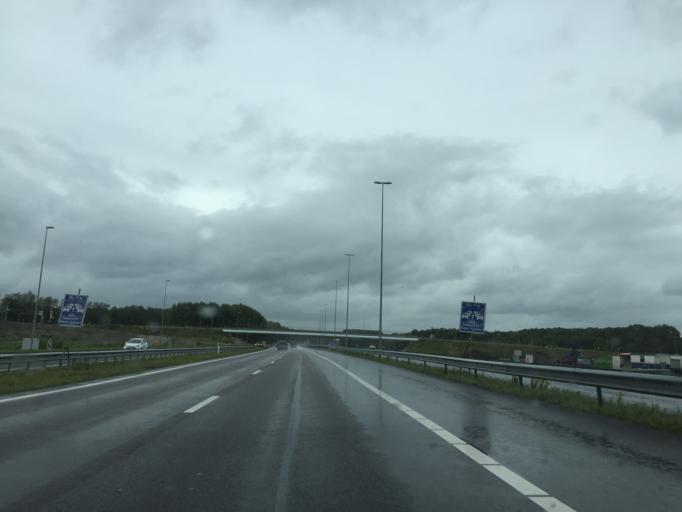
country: NL
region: Flevoland
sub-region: Gemeente Almere
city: Almere Stad
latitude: 52.3487
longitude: 5.1922
